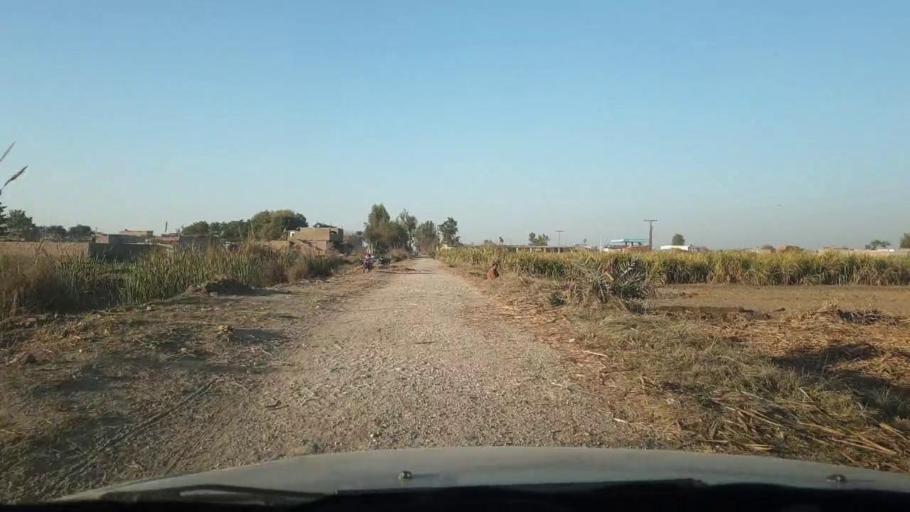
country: PK
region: Sindh
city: Ghotki
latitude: 27.9923
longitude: 69.2725
